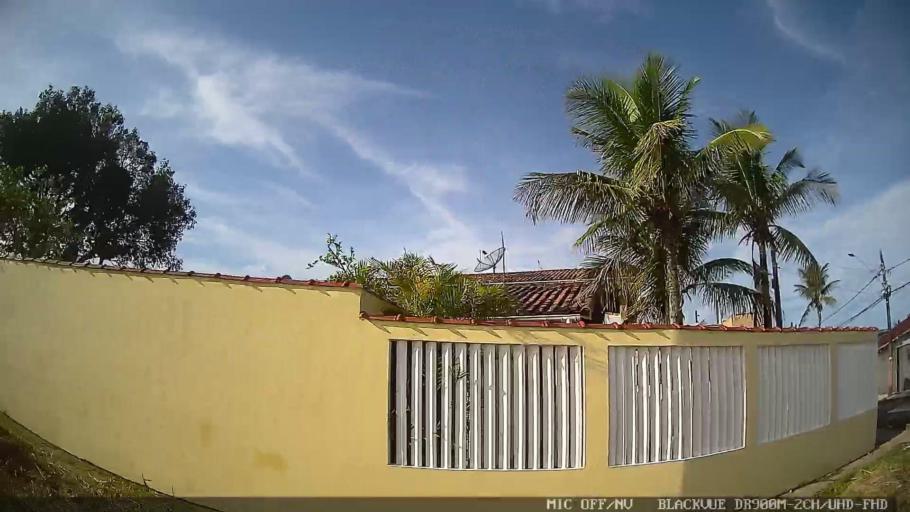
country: BR
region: Sao Paulo
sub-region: Itanhaem
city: Itanhaem
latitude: -24.1609
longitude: -46.7559
